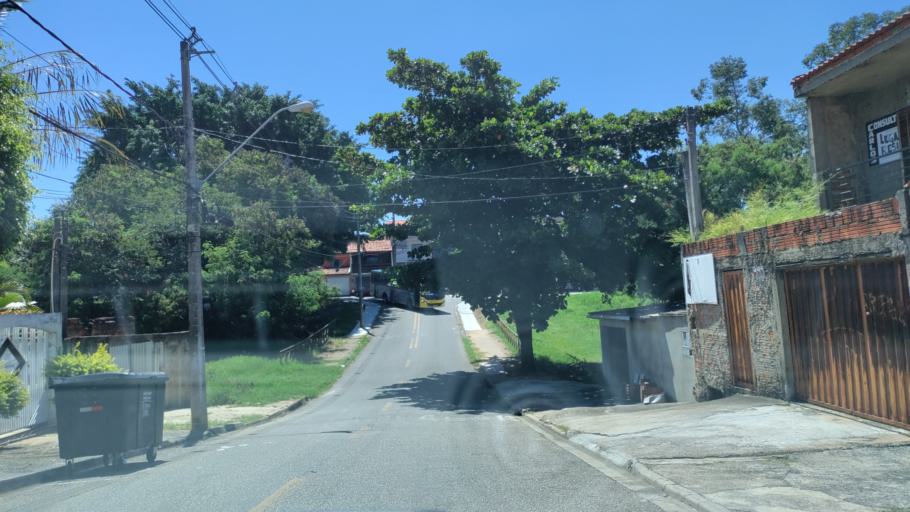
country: BR
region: Sao Paulo
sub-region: Sorocaba
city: Sorocaba
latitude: -23.4591
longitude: -47.4751
